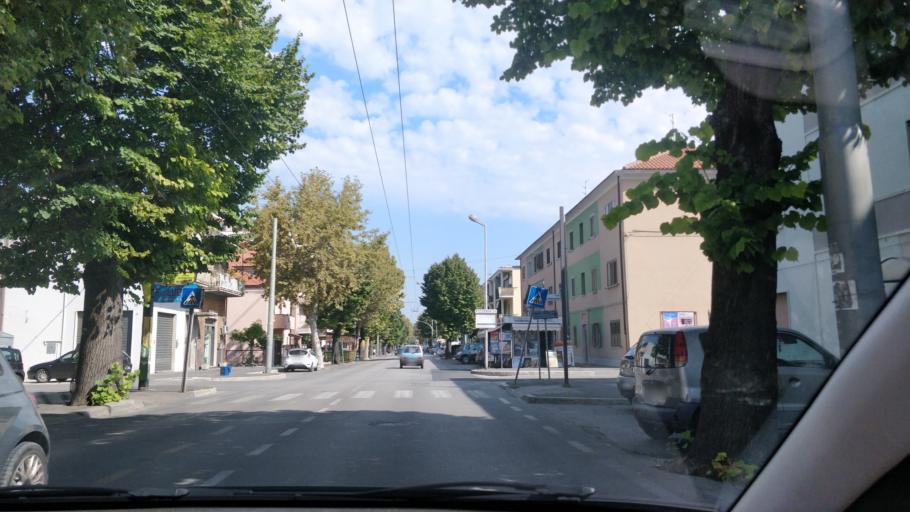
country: IT
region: Abruzzo
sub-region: Provincia di Chieti
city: Chieti
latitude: 42.3678
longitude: 14.1423
